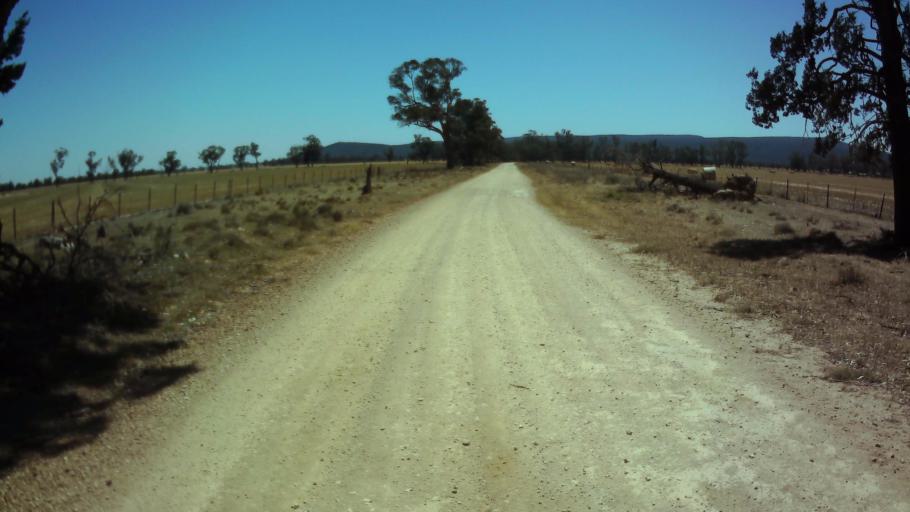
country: AU
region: New South Wales
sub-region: Weddin
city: Grenfell
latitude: -34.0263
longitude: 147.9617
